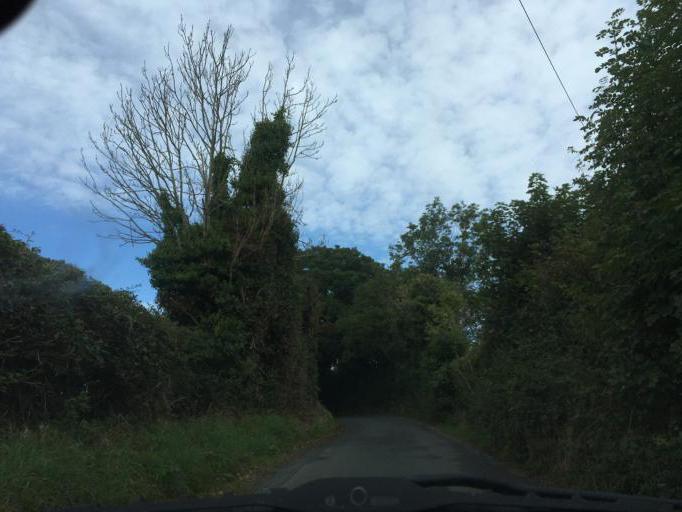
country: IE
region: Leinster
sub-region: Wicklow
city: Rathnew
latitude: 52.9228
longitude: -6.1042
